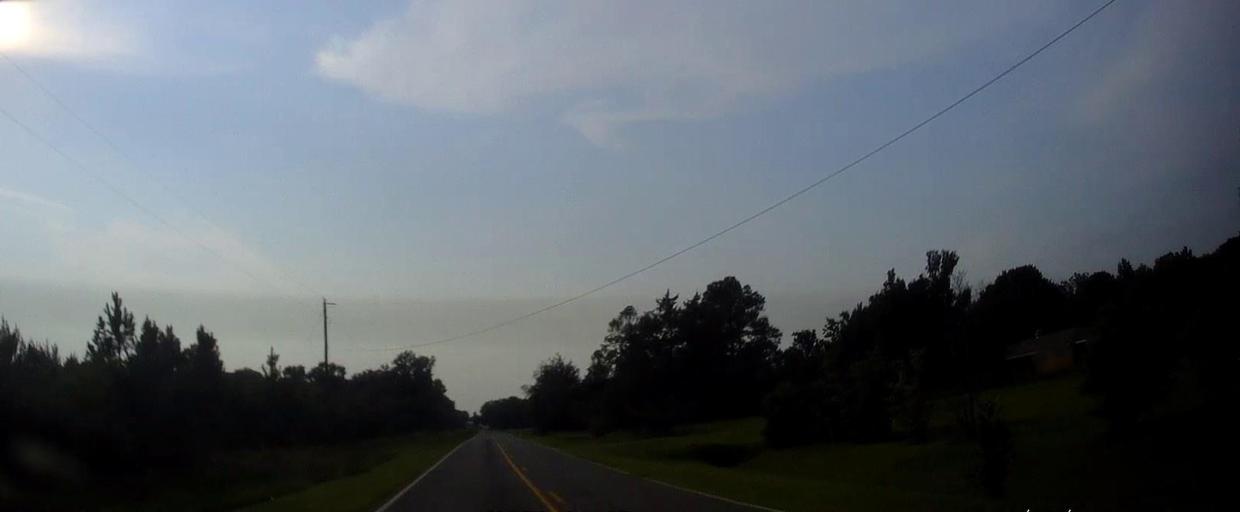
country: US
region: Georgia
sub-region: Laurens County
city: Dublin
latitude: 32.4865
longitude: -82.9755
